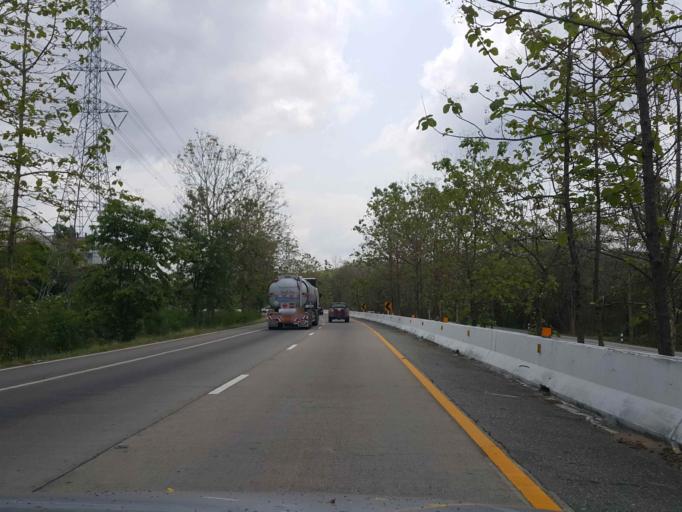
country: TH
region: Lamphun
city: Mae Tha
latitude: 18.5105
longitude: 99.0973
